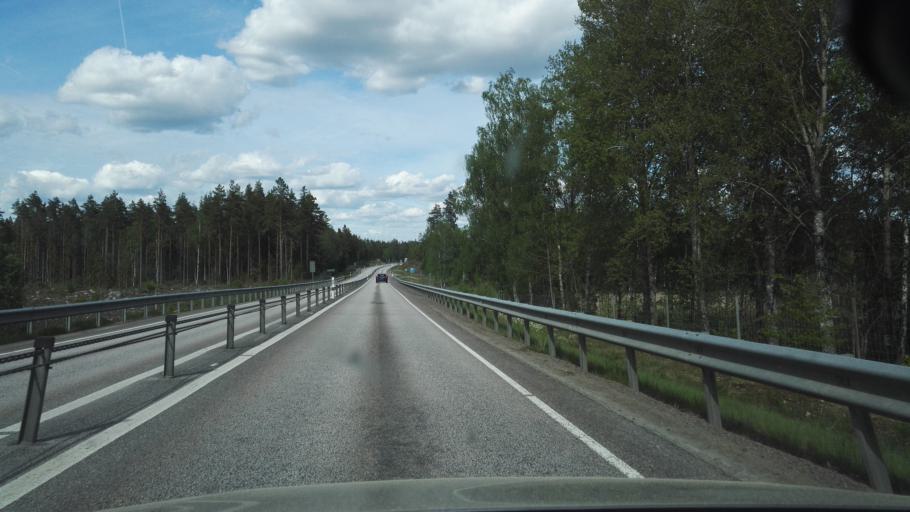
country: SE
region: Kronoberg
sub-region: Vaxjo Kommun
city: Braas
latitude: 56.9890
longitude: 14.9946
